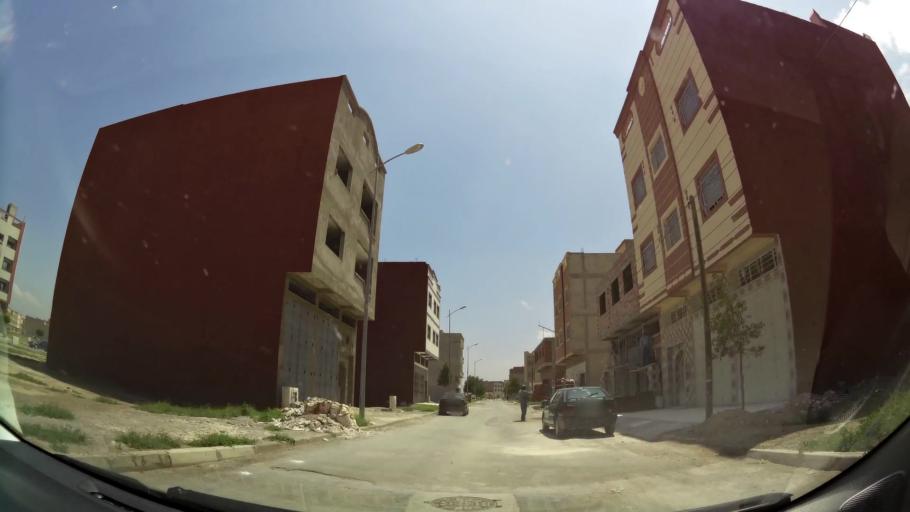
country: MA
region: Oriental
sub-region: Oujda-Angad
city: Oujda
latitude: 34.6930
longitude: -1.8928
